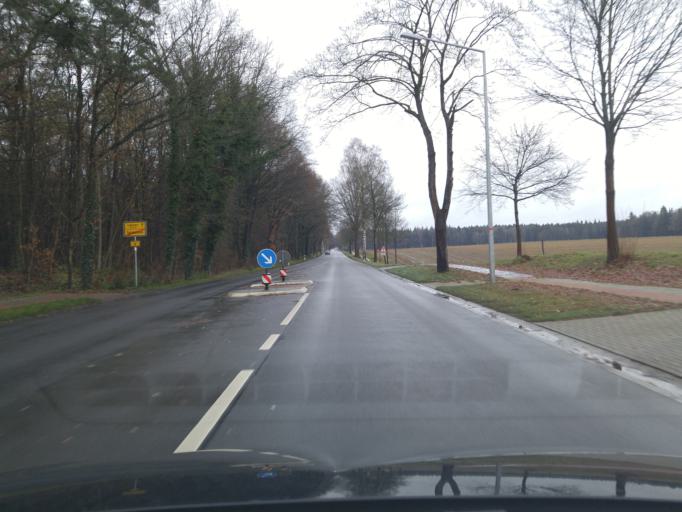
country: DE
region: Lower Saxony
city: Sprakensehl
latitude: 52.7709
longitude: 10.4933
